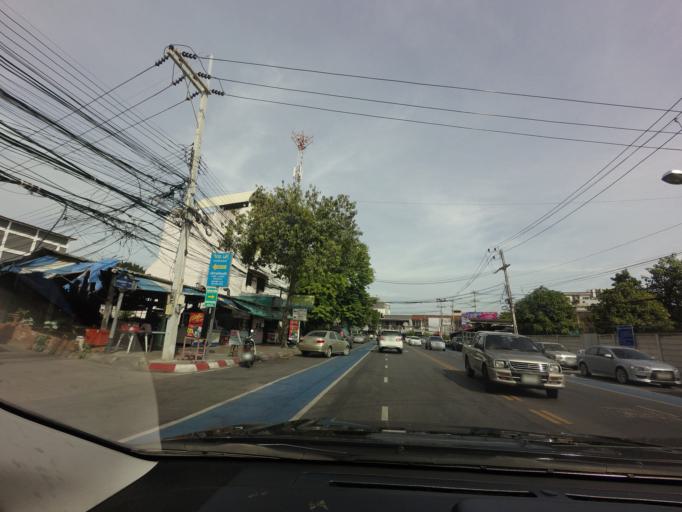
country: TH
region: Chon Buri
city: Chon Buri
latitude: 13.2855
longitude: 100.9175
